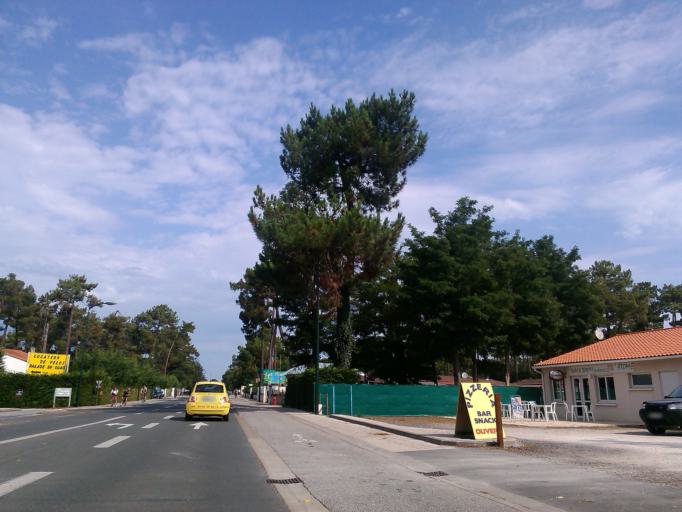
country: FR
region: Poitou-Charentes
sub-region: Departement de la Charente-Maritime
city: La Tremblade
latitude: 45.7880
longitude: -1.1584
